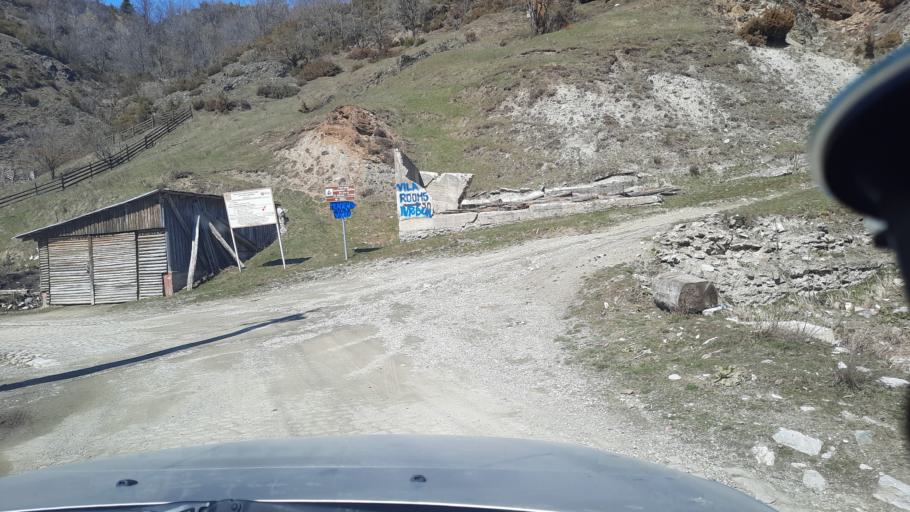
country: MK
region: Gostivar
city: Vrutok
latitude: 41.7211
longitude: 20.7329
